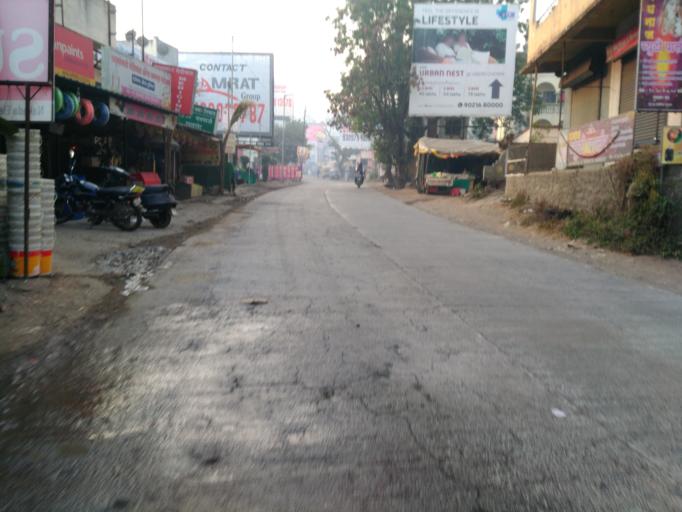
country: IN
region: Maharashtra
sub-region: Pune Division
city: Pune
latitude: 18.4584
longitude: 73.9123
